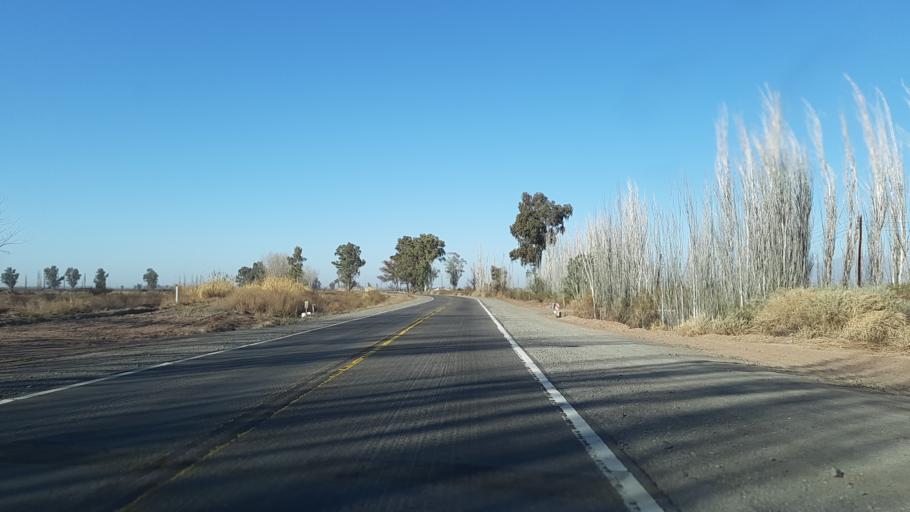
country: AR
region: Mendoza
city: General Lavalle
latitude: -32.5424
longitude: -68.6522
